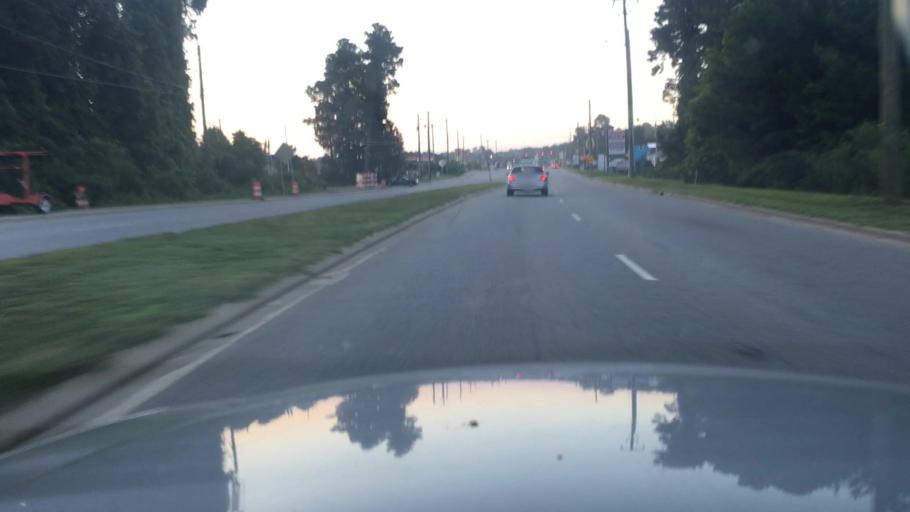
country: US
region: North Carolina
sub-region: Cumberland County
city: Fort Bragg
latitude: 35.0630
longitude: -79.0189
